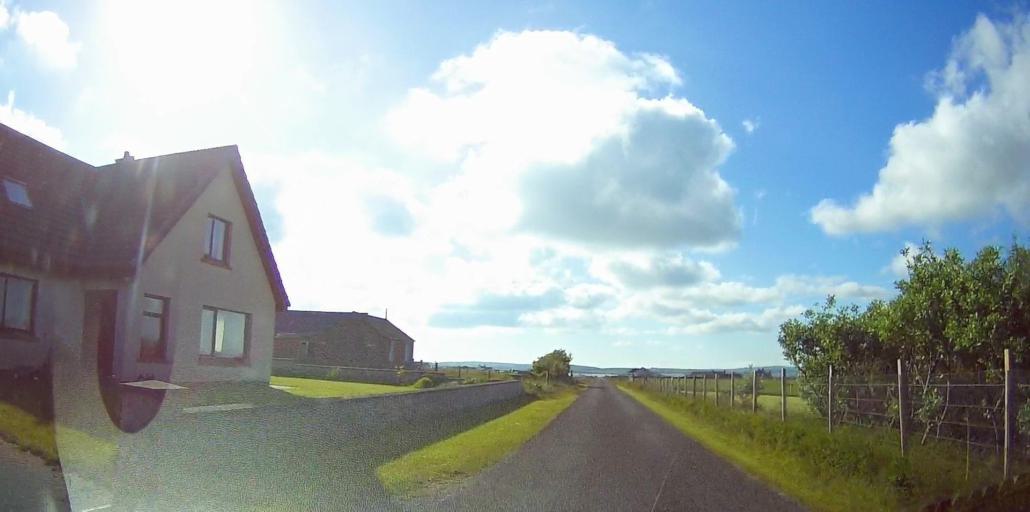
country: GB
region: Scotland
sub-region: Orkney Islands
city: Stromness
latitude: 58.9860
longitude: -3.1914
